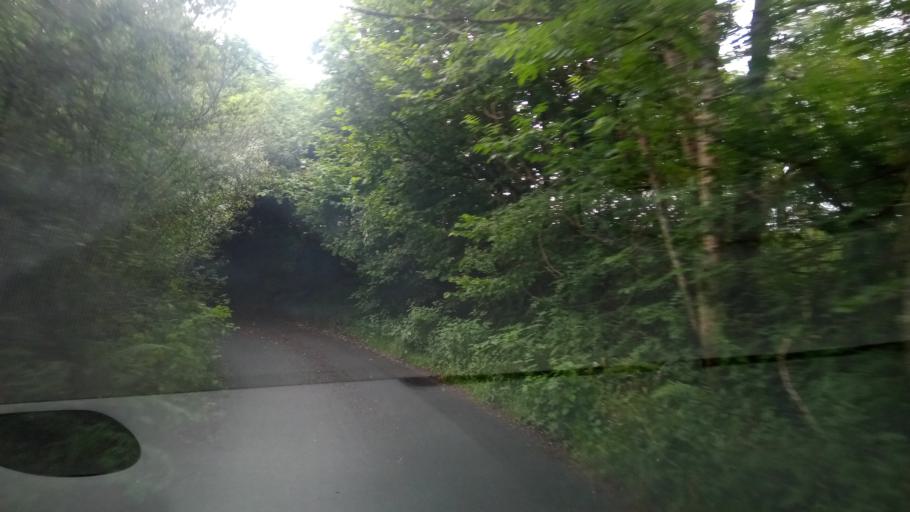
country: GB
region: England
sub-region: Cumbria
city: Kirkby Stephen
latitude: 54.4202
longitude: -2.3392
